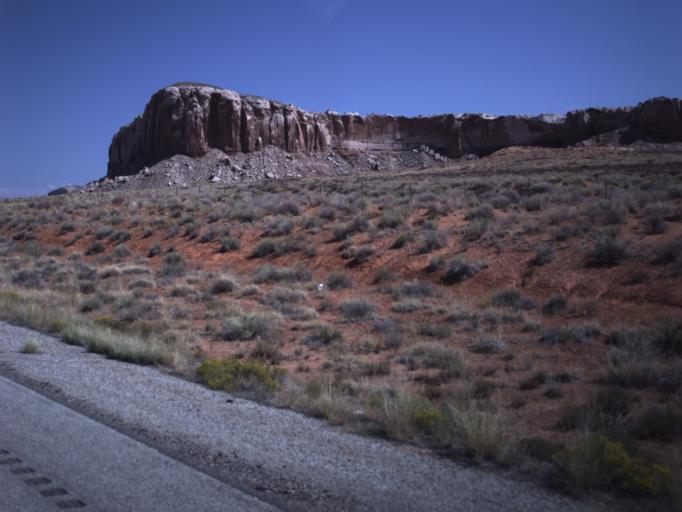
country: US
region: Utah
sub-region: San Juan County
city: Blanding
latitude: 37.2279
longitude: -109.6172
